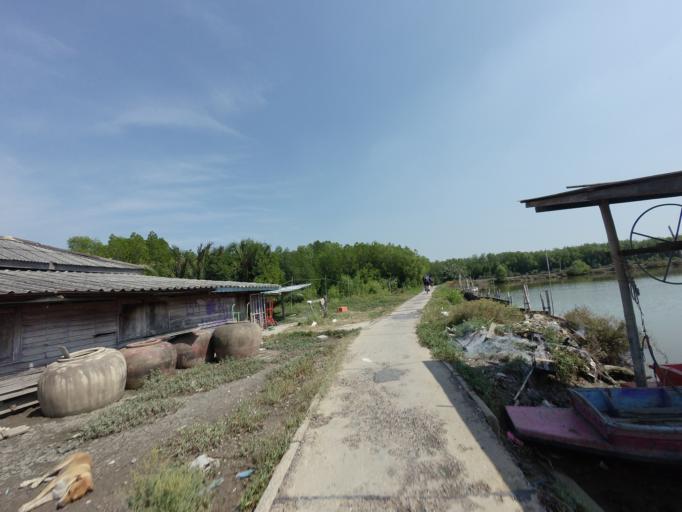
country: TH
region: Bangkok
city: Thung Khru
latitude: 13.5260
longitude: 100.4211
